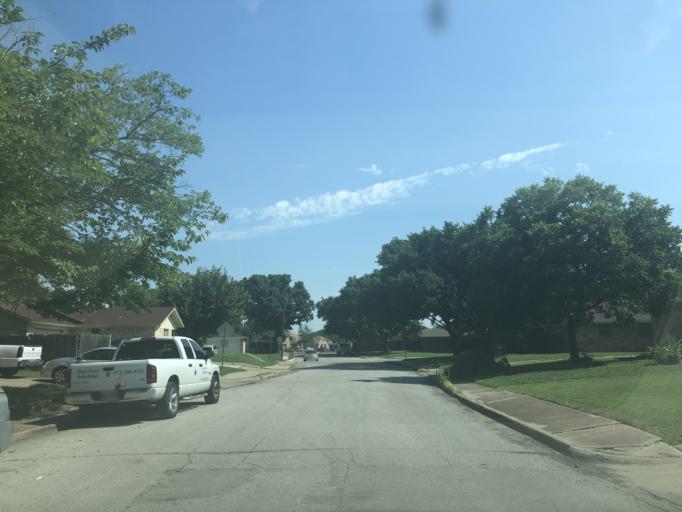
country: US
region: Texas
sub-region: Dallas County
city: Grand Prairie
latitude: 32.7237
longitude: -97.0014
